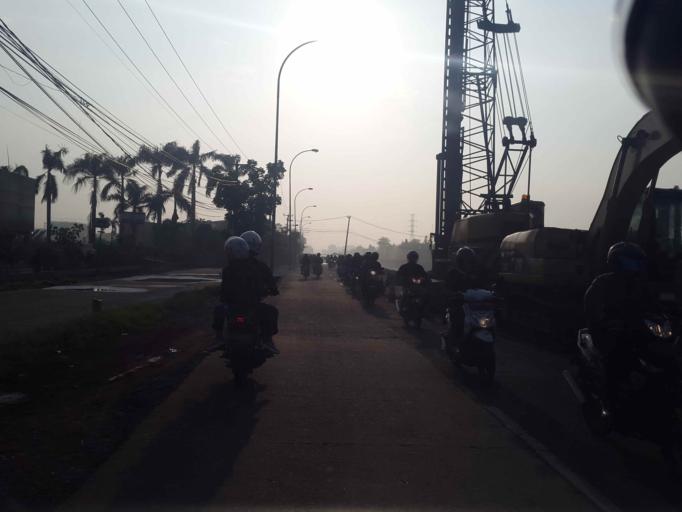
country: ID
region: West Java
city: Bekasi
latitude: -6.2671
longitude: 107.0351
